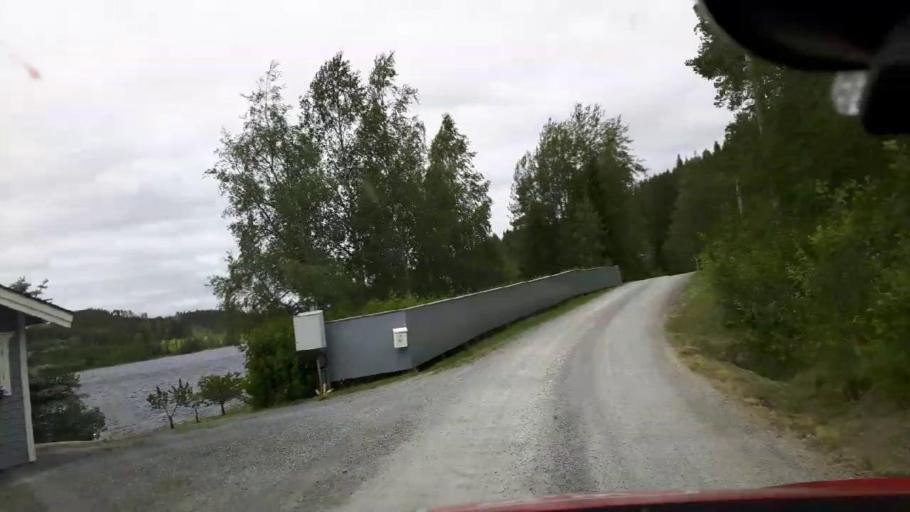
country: SE
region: Jaemtland
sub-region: OEstersunds Kommun
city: Brunflo
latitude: 63.0220
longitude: 14.9415
